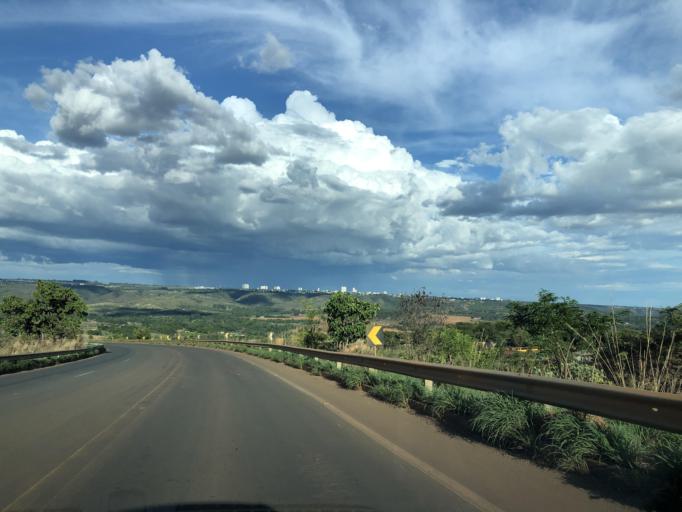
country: BR
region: Goias
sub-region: Luziania
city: Luziania
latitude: -16.0150
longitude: -48.1386
